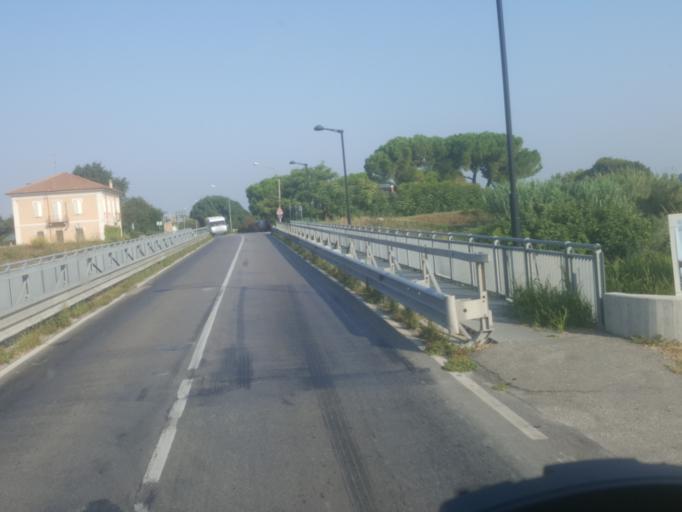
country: IT
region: Emilia-Romagna
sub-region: Provincia di Ravenna
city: Mezzano
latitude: 44.4694
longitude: 12.0832
